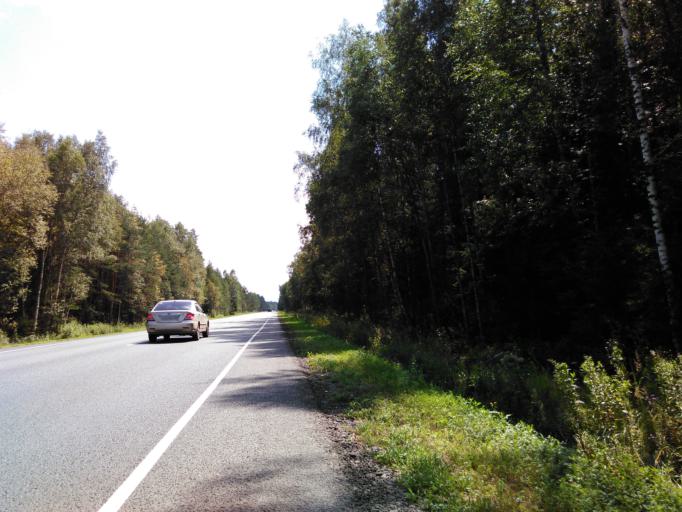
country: RU
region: Moskovskaya
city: Elektrogorsk
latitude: 56.0355
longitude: 38.7462
